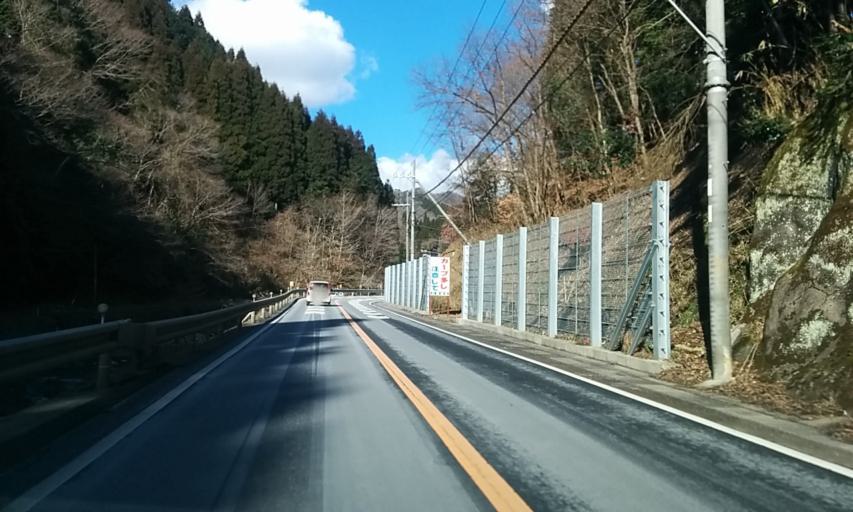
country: JP
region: Kyoto
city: Fukuchiyama
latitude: 35.3483
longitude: 135.0627
